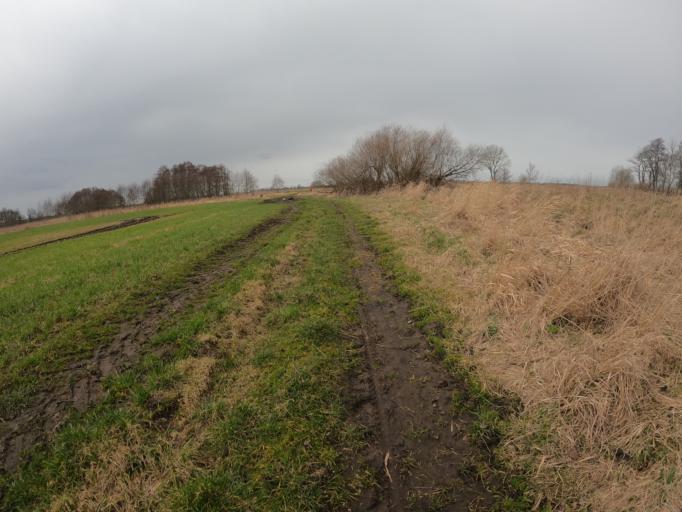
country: PL
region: West Pomeranian Voivodeship
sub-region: Powiat gryficki
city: Trzebiatow
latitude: 54.0750
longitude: 15.2410
